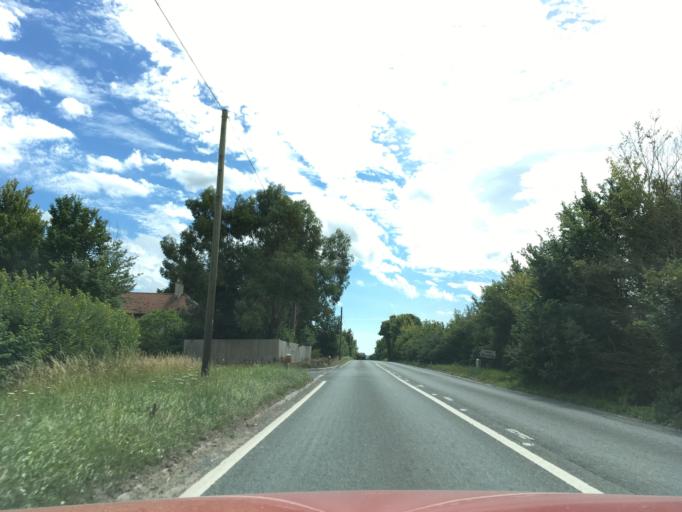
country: GB
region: England
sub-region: Somerset
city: Ilchester
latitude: 51.0407
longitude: -2.6545
